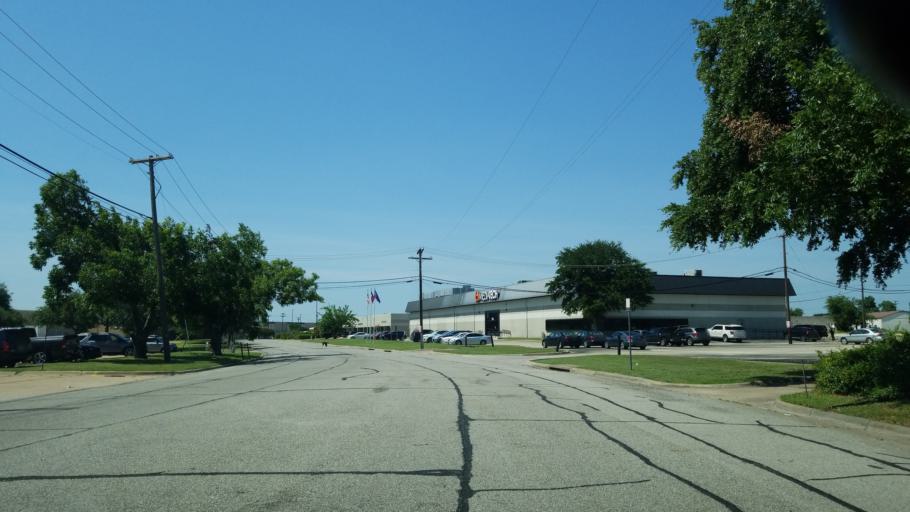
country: US
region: Texas
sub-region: Dallas County
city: Farmers Branch
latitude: 32.9233
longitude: -96.9028
